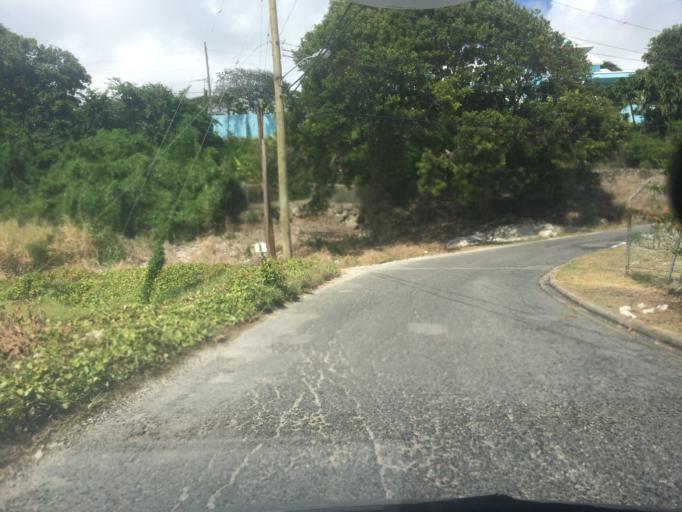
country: BB
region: Christ Church
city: Oistins
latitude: 13.0662
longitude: -59.5097
